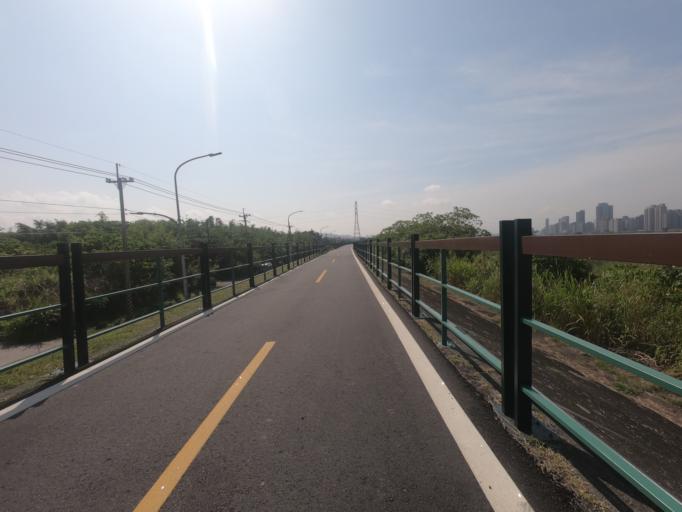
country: TW
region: Taipei
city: Taipei
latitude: 25.1017
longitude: 121.4857
